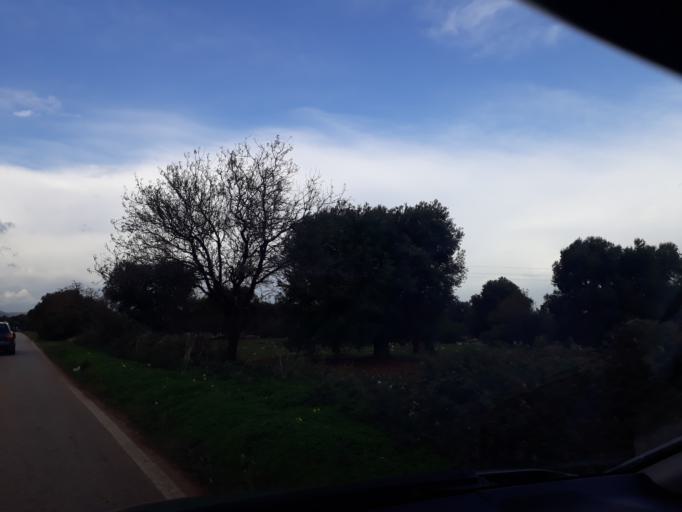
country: IT
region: Apulia
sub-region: Provincia di Brindisi
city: Pezze di Greco
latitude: 40.7968
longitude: 17.4124
